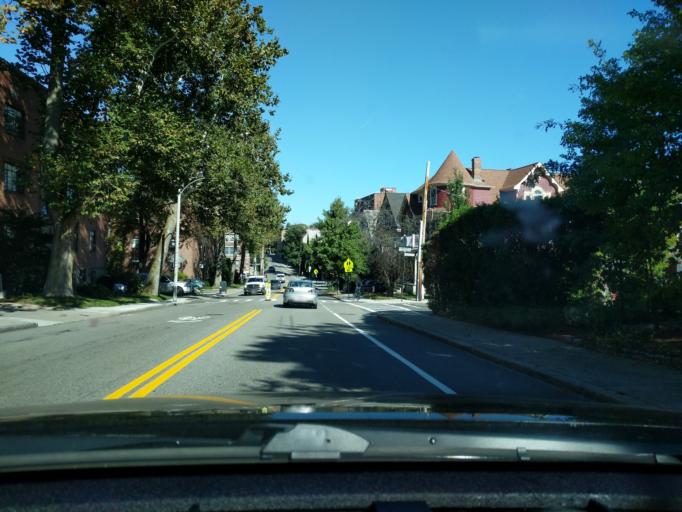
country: US
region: Massachusetts
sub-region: Norfolk County
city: Brookline
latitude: 42.3388
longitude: -71.1181
